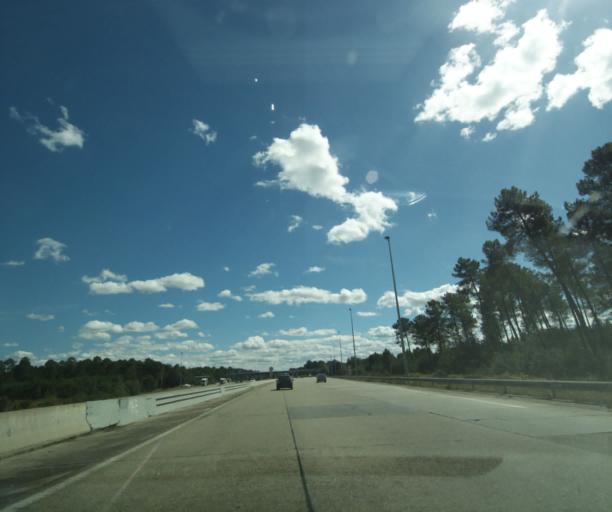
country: FR
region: Aquitaine
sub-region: Departement de la Gironde
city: Saint-Selve
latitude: 44.6617
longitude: -0.4580
